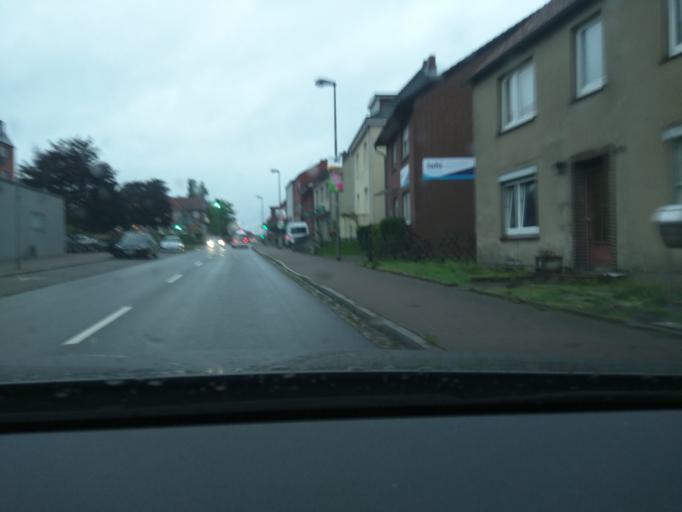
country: DE
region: Schleswig-Holstein
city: Lauenburg
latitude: 53.3750
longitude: 10.5573
